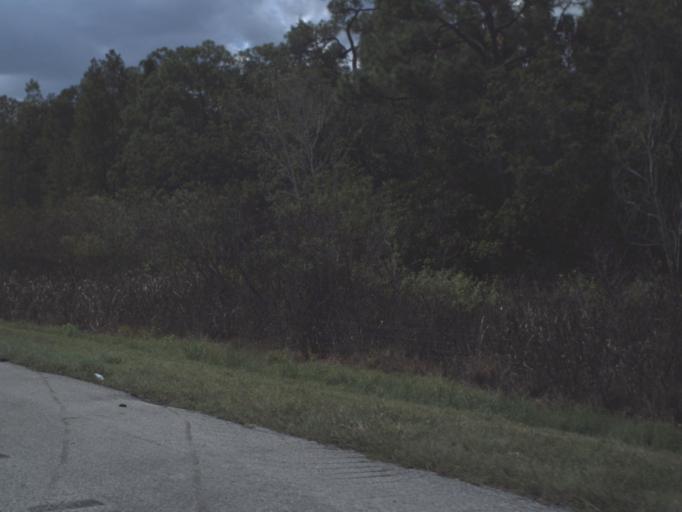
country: US
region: Florida
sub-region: Polk County
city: Davenport
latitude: 28.2078
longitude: -81.6856
